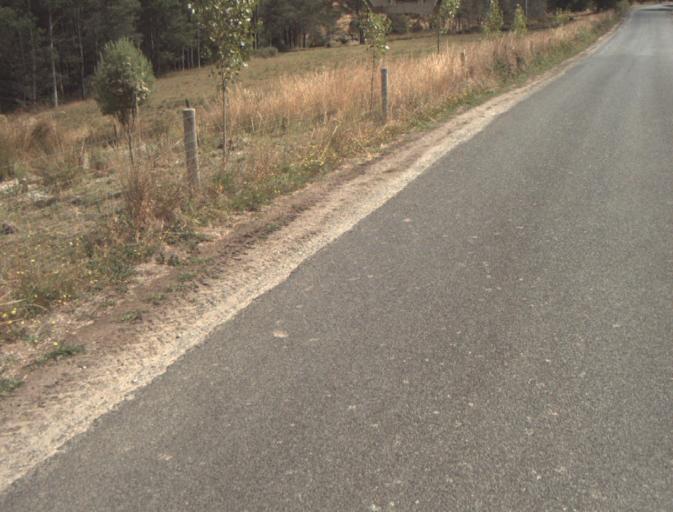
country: AU
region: Tasmania
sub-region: Launceston
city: Mayfield
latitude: -41.2590
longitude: 147.2076
